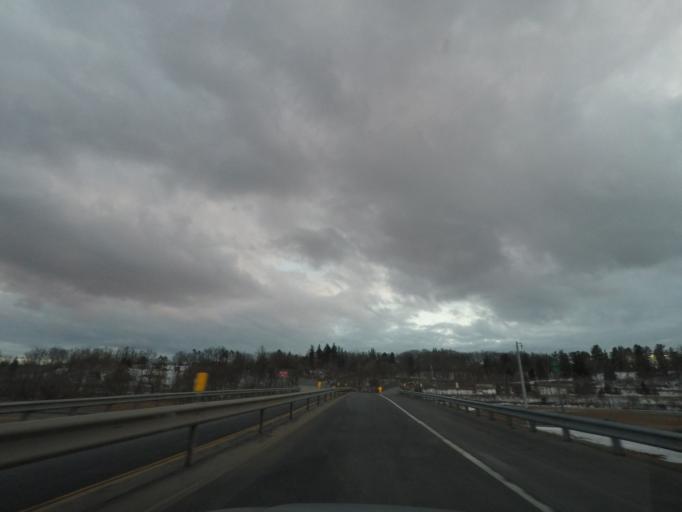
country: US
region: New York
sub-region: Montgomery County
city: Fonda
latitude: 42.9456
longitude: -74.3595
